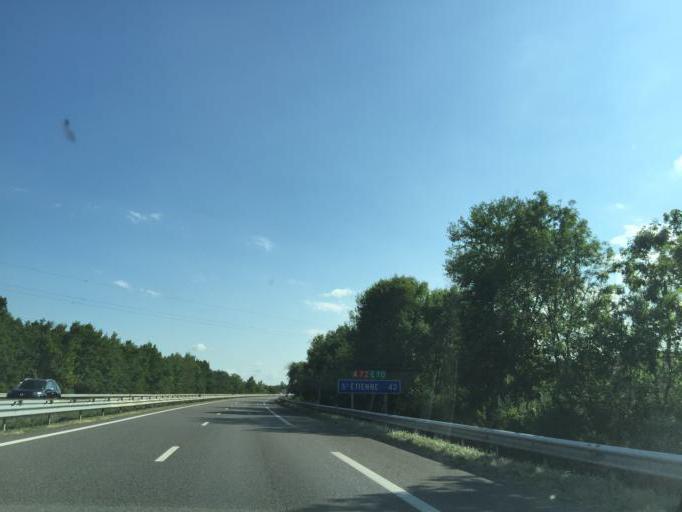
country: FR
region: Rhone-Alpes
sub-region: Departement de la Loire
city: Feurs
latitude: 45.7291
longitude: 4.1821
